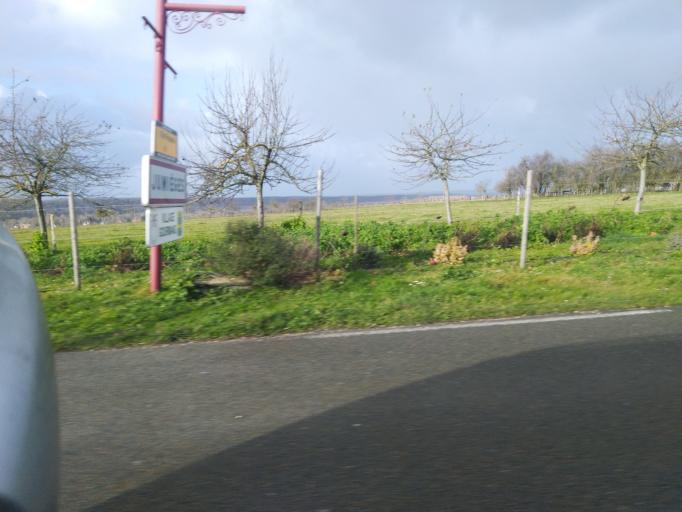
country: FR
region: Haute-Normandie
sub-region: Departement de la Seine-Maritime
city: Jumieges
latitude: 49.4387
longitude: 0.8245
